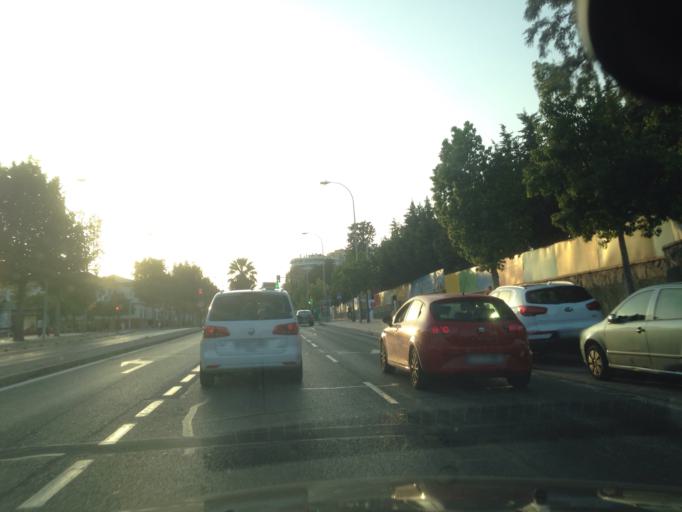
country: ES
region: Andalusia
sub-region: Provincia de Malaga
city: Malaga
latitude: 36.7188
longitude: -4.4455
